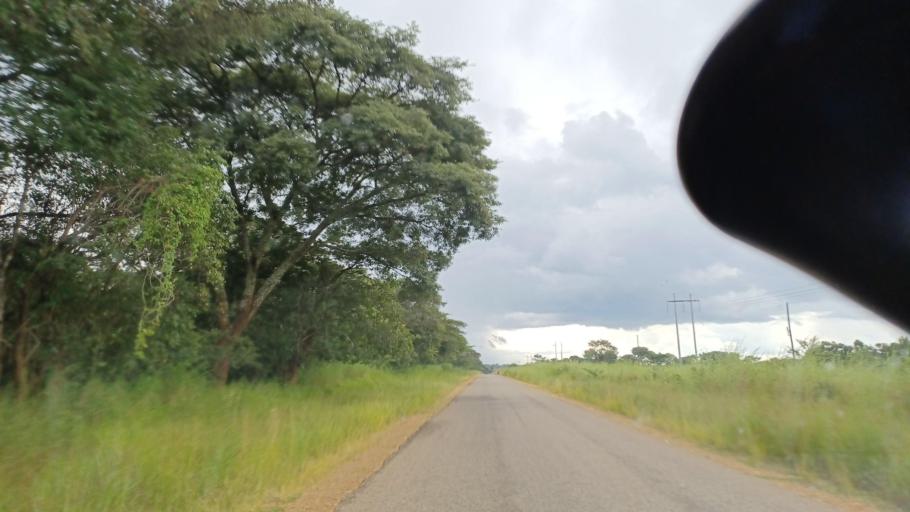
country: ZM
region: North-Western
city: Kasempa
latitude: -13.0036
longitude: 26.0119
